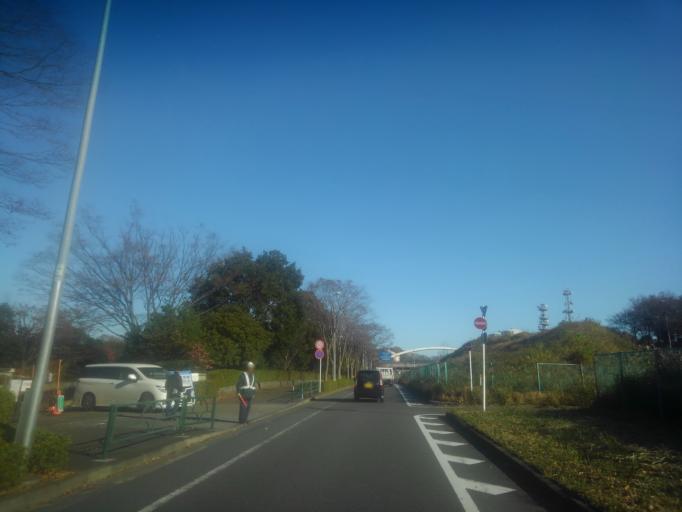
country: JP
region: Tokyo
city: Hino
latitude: 35.6239
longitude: 139.4608
